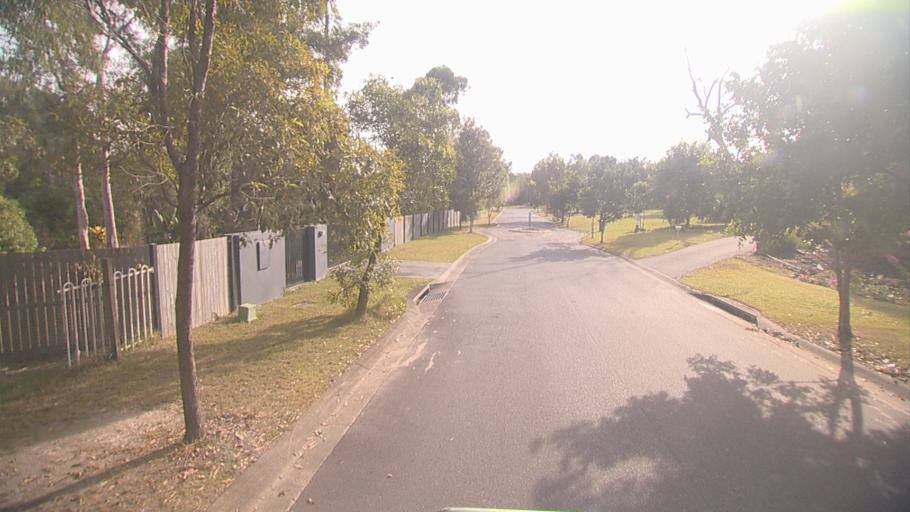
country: AU
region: Queensland
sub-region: Brisbane
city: Forest Lake
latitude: -27.6591
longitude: 153.0163
